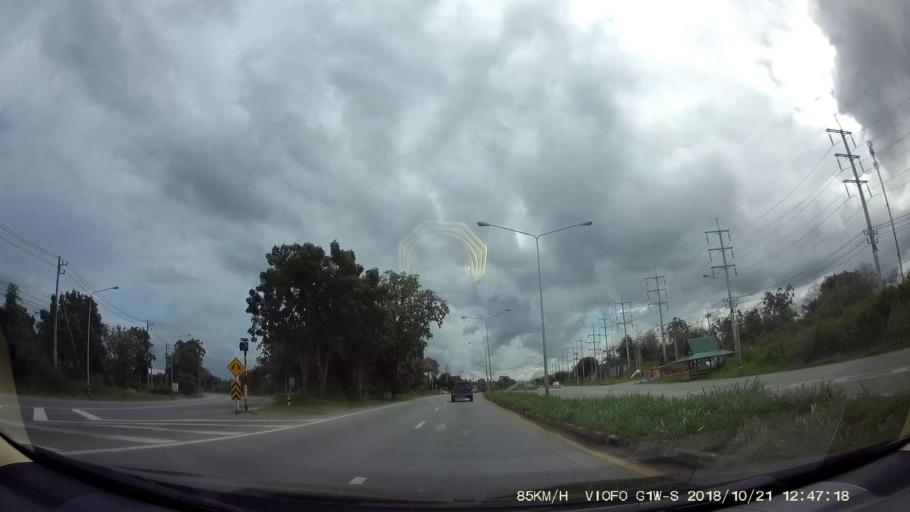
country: TH
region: Nakhon Ratchasima
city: Amphoe Sikhiu
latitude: 14.9301
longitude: 101.6839
